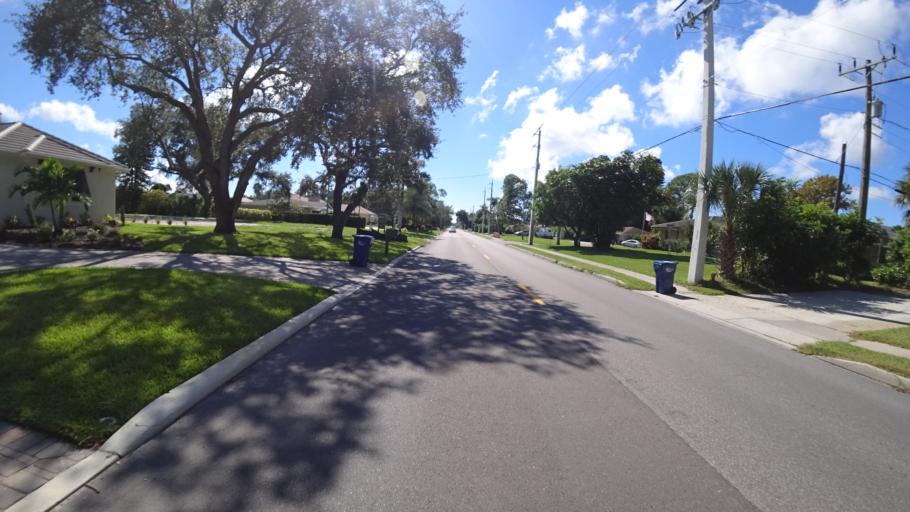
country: US
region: Florida
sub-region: Manatee County
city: West Bradenton
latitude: 27.4867
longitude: -82.6121
